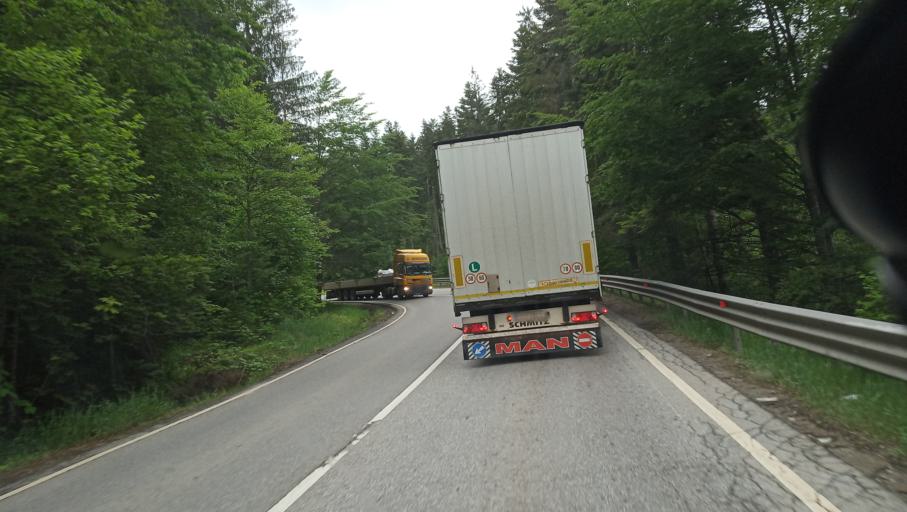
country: RO
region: Neamt
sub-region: Comuna Pipirig
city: Dolhesti
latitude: 47.1656
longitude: 26.0111
